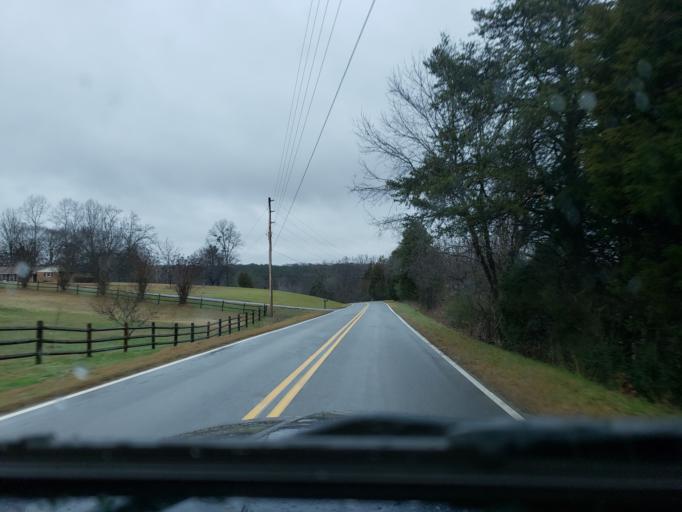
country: US
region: North Carolina
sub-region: Cleveland County
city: White Plains
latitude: 35.1795
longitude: -81.3700
